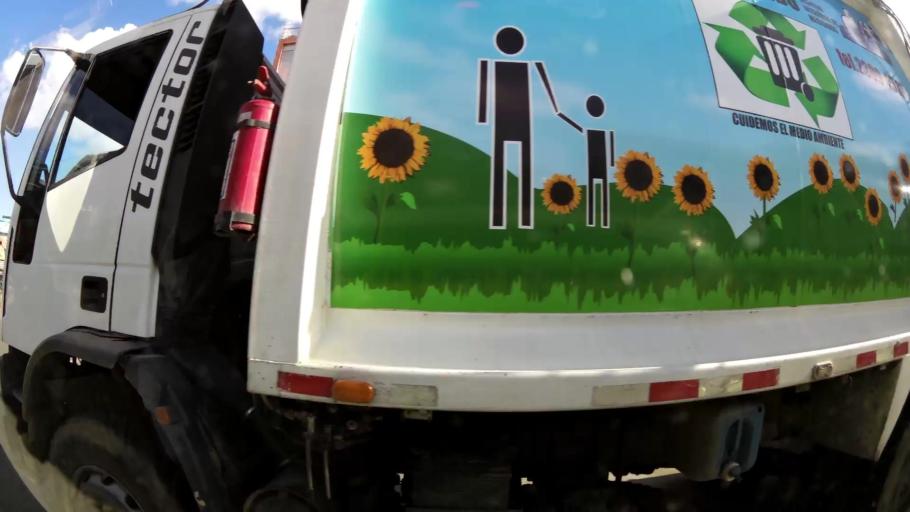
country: UY
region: Montevideo
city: Montevideo
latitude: -34.8715
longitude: -56.1903
